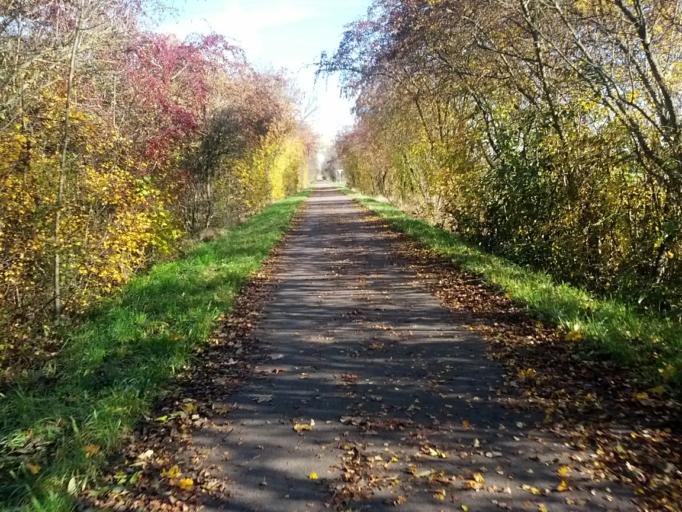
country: DE
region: Thuringia
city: Sonneborn
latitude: 50.9974
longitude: 10.5800
